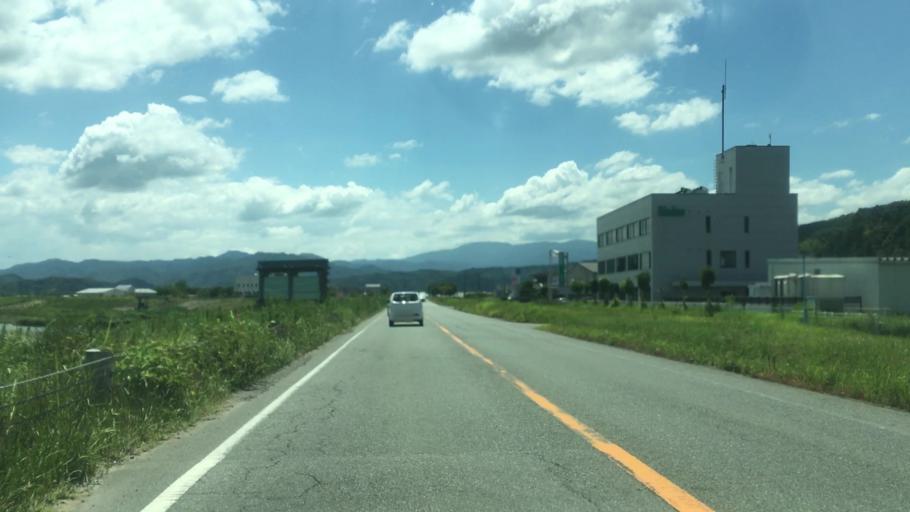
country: JP
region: Hyogo
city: Toyooka
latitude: 35.5034
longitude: 134.8107
